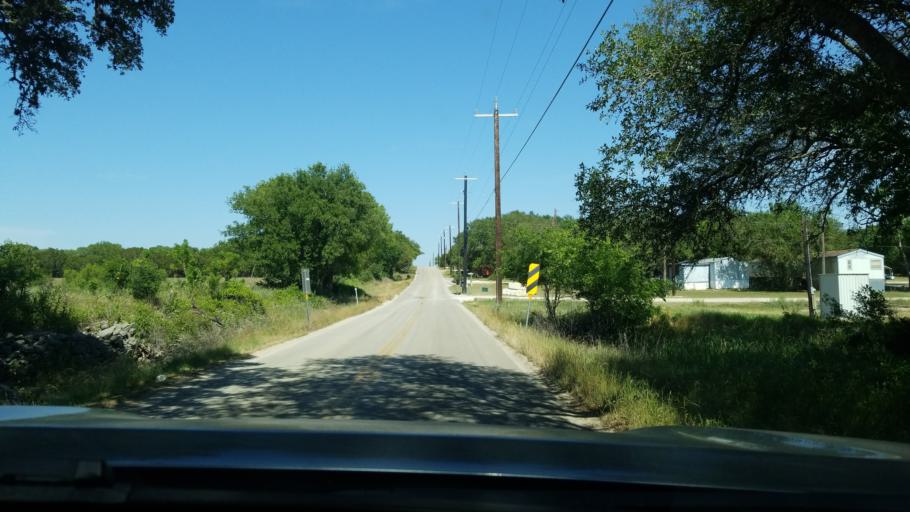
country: US
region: Texas
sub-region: Comal County
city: Bulverde
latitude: 29.7590
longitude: -98.5034
